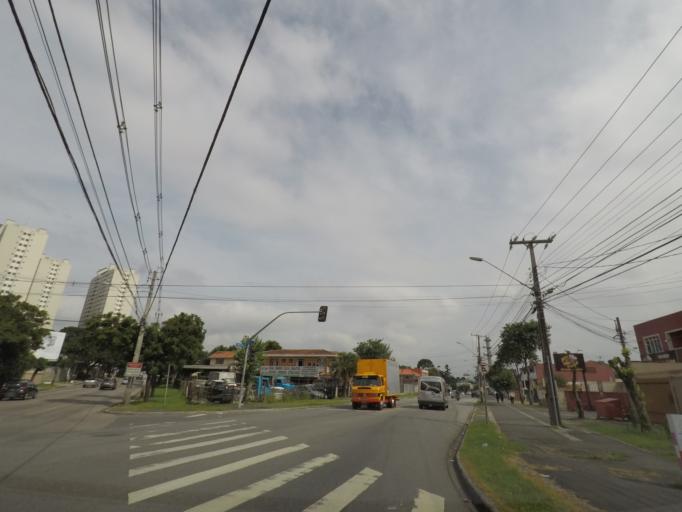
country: BR
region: Parana
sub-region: Curitiba
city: Curitiba
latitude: -25.4965
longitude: -49.2964
